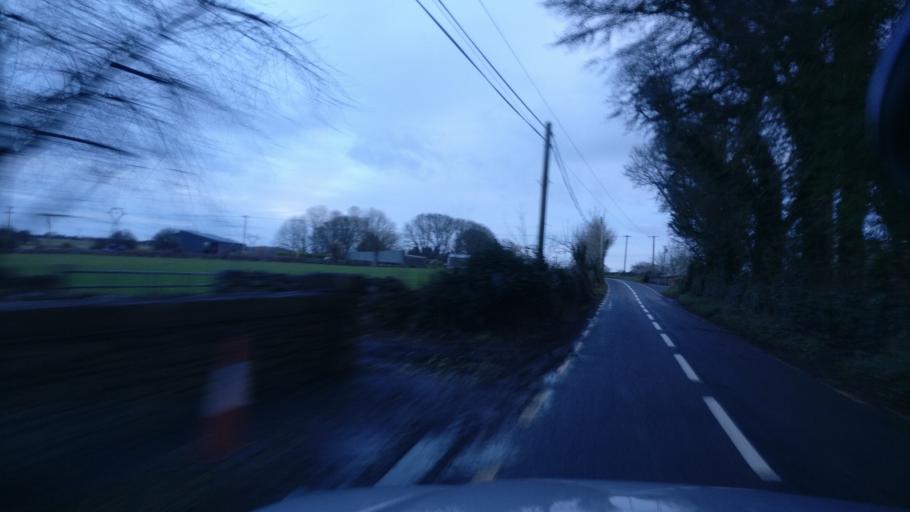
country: IE
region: Connaught
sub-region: County Galway
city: Athenry
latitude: 53.2540
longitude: -8.6763
